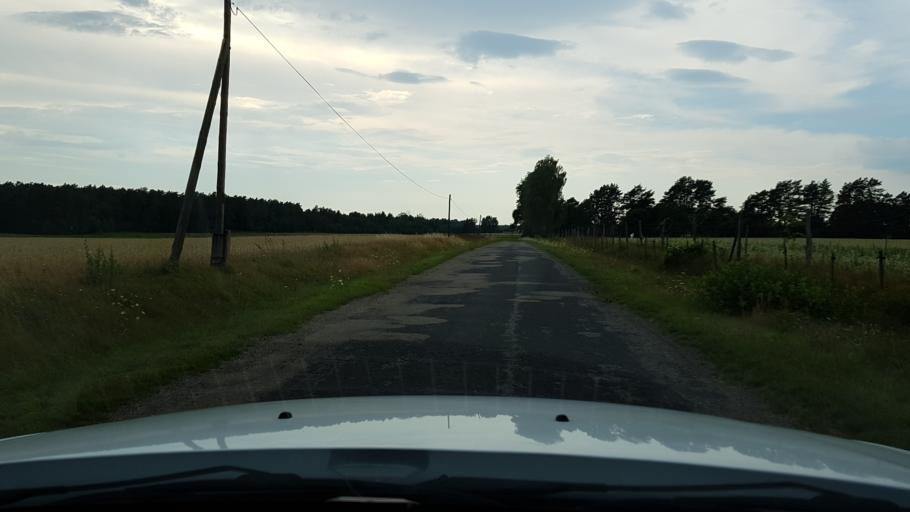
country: PL
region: West Pomeranian Voivodeship
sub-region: Powiat drawski
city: Czaplinek
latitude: 53.4335
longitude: 16.2910
